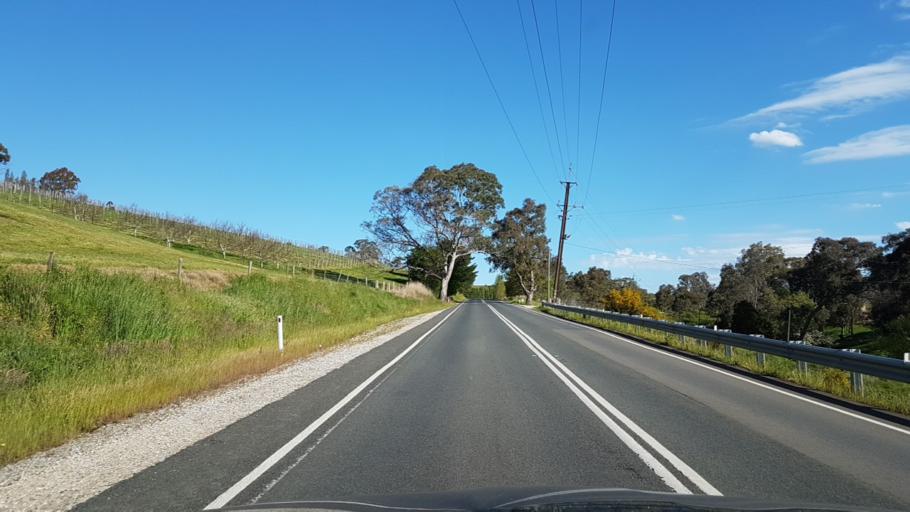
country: AU
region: South Australia
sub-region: Adelaide Hills
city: Gumeracha
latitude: -34.8379
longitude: 138.8930
